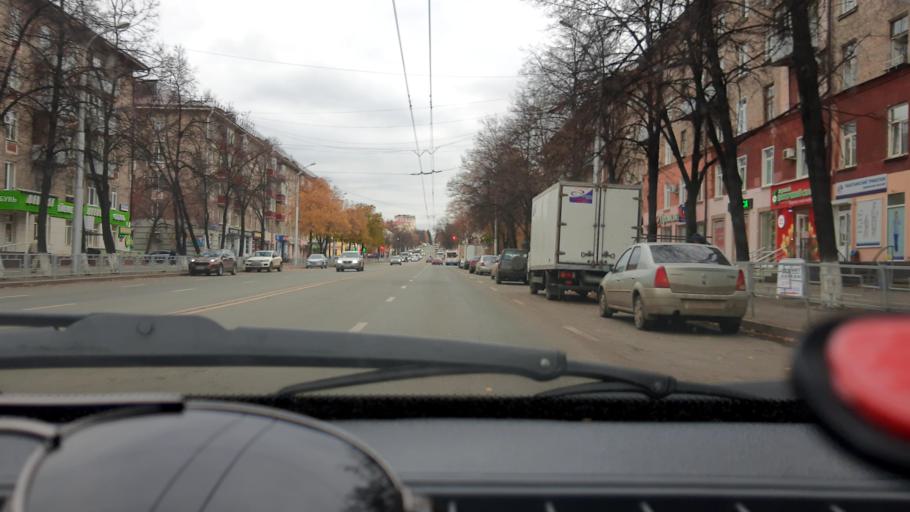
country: RU
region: Bashkortostan
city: Ufa
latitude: 54.8142
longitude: 56.0870
